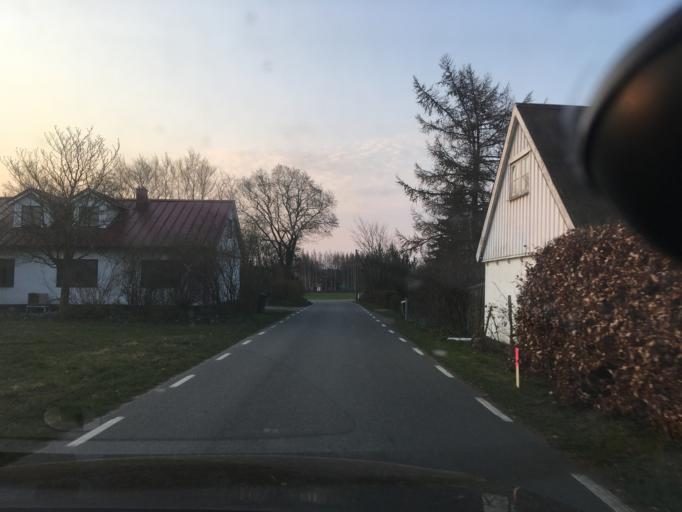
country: SE
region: Skane
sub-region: Ystads Kommun
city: Kopingebro
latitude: 55.4010
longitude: 14.1637
